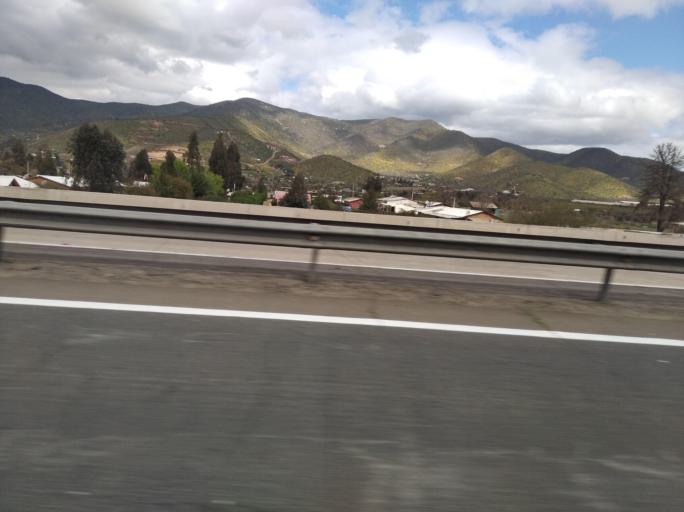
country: CL
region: Santiago Metropolitan
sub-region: Provincia de Melipilla
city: Melipilla
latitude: -33.4125
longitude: -71.1487
